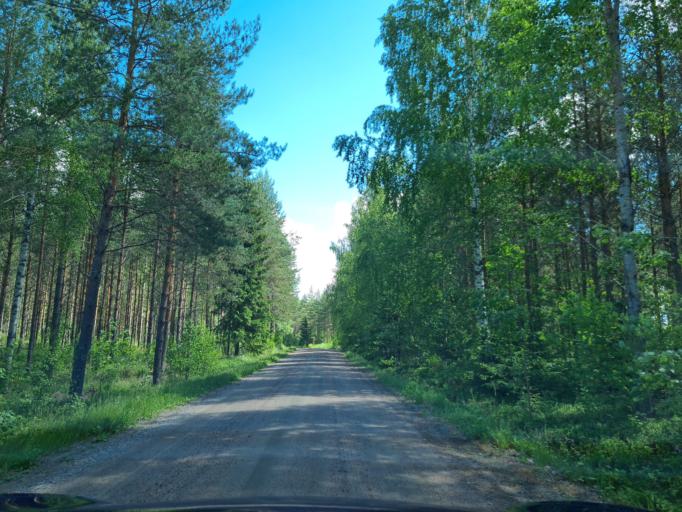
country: FI
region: Uusimaa
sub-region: Helsinki
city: Kaerkoelae
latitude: 60.7544
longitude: 23.9577
